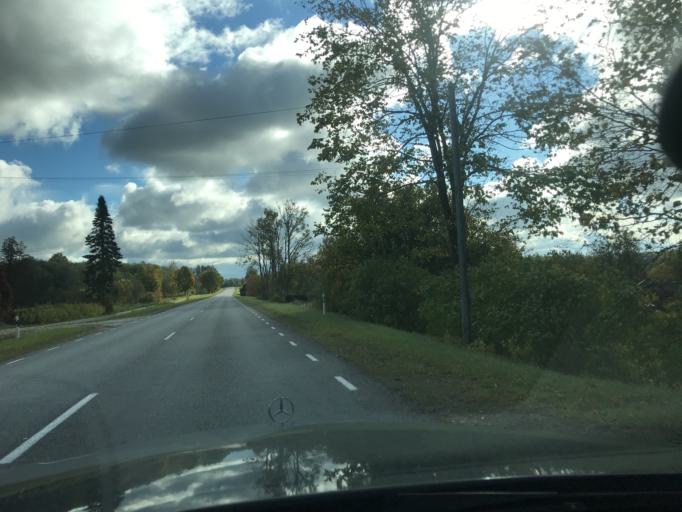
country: EE
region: Vorumaa
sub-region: Antsla vald
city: Vana-Antsla
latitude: 57.9481
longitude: 26.2926
